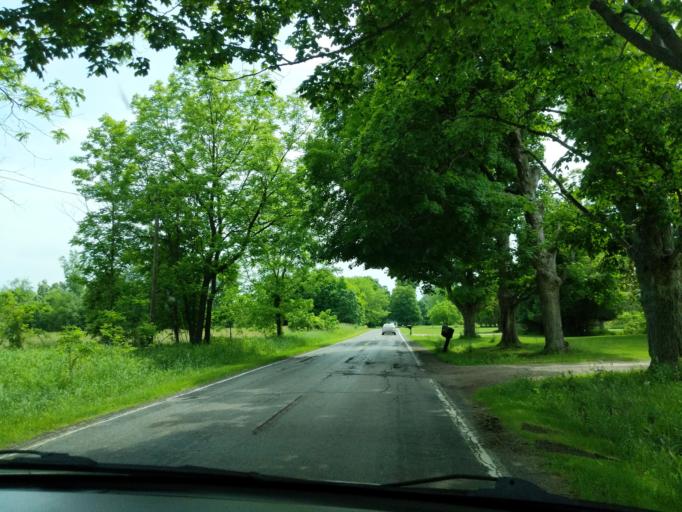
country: US
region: Michigan
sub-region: Ingham County
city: Williamston
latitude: 42.6935
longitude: -84.2418
